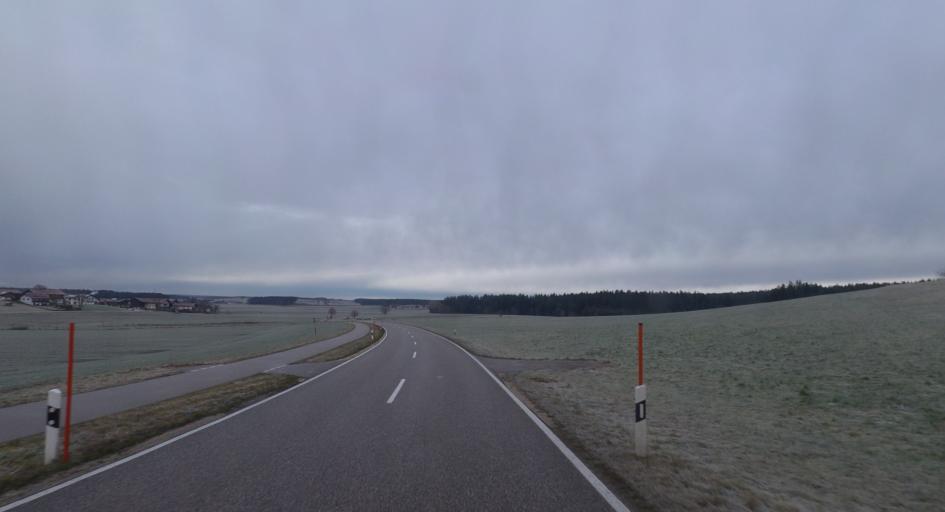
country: DE
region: Bavaria
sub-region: Upper Bavaria
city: Nussdorf
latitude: 47.9271
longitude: 12.6511
